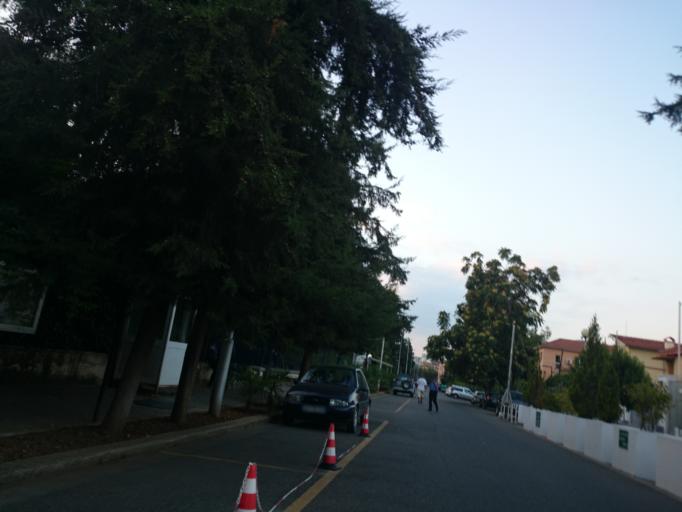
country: AL
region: Tirane
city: Tirana
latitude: 41.3306
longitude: 19.8078
